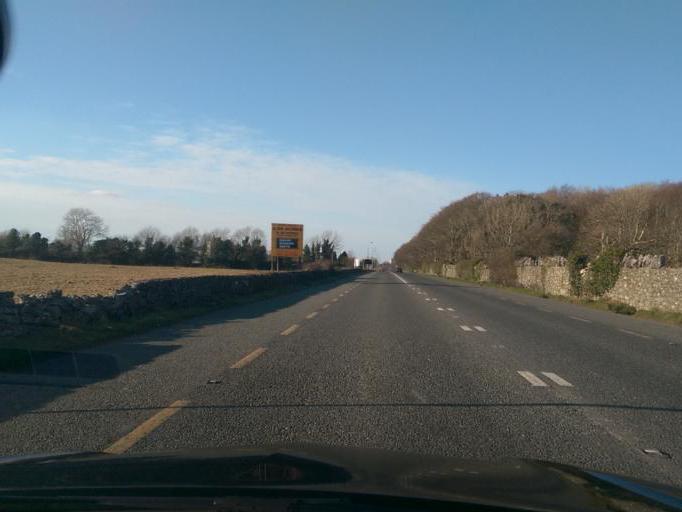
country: IE
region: Connaught
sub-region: County Galway
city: Oranmore
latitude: 53.2215
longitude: -8.8750
